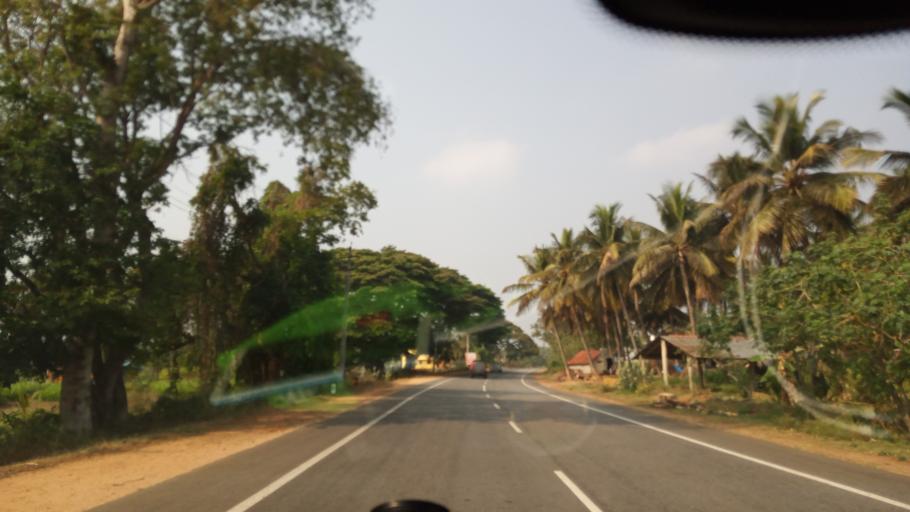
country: IN
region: Karnataka
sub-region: Mandya
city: Nagamangala
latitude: 12.7611
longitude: 76.7342
